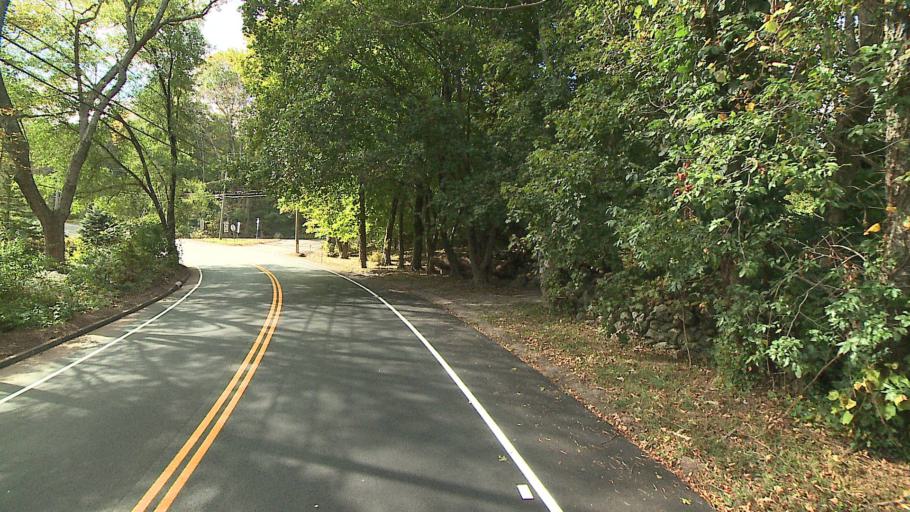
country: US
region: Connecticut
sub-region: New Haven County
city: Prospect
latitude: 41.4534
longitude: -72.9891
